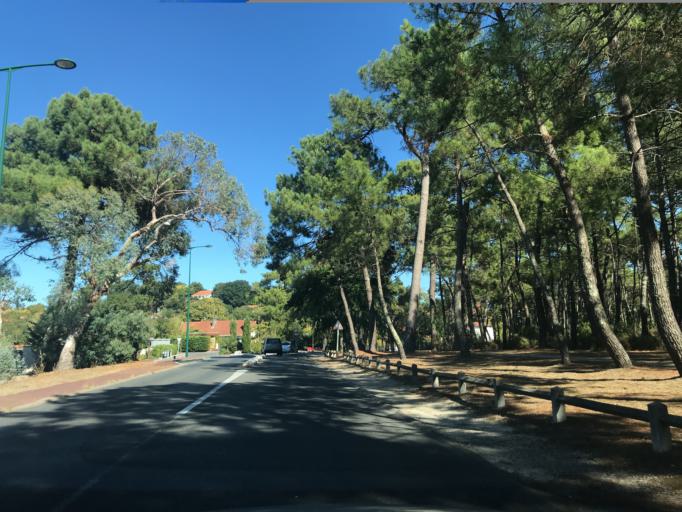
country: FR
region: Aquitaine
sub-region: Departement de la Gironde
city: Arcachon
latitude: 44.6545
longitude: -1.1797
